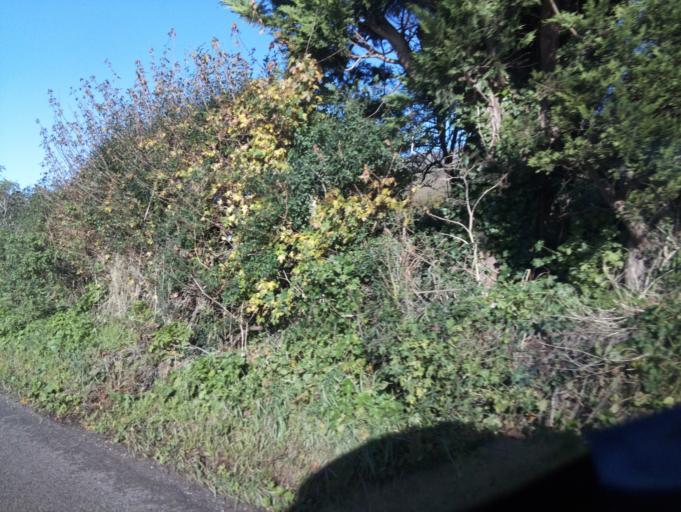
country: GB
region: England
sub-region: Somerset
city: Langport
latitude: 51.0560
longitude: -2.8507
